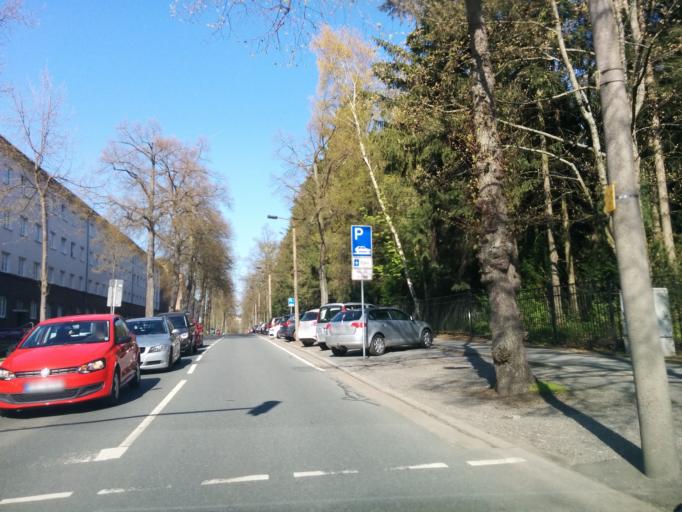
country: DE
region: Saxony
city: Chemnitz
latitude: 50.8128
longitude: 12.9320
